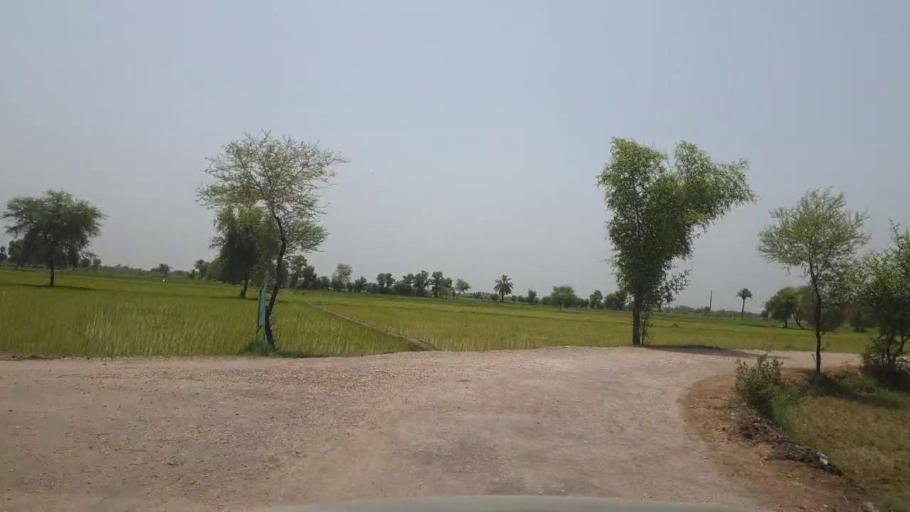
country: PK
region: Sindh
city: Garhi Yasin
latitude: 27.9208
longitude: 68.3703
